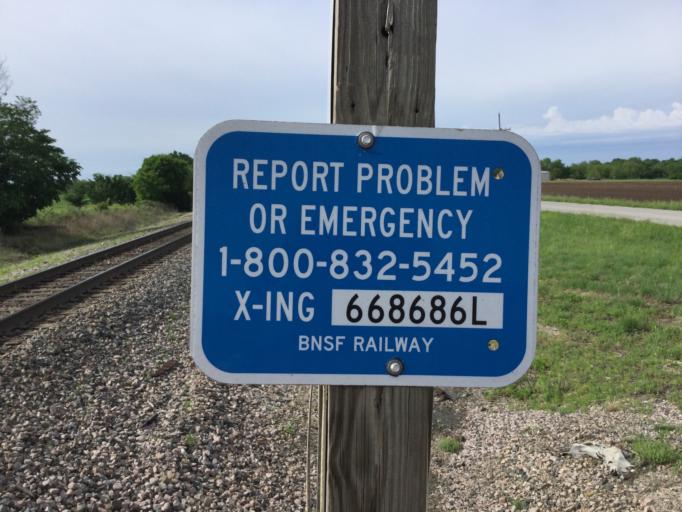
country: US
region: Kansas
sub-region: Linn County
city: Pleasanton
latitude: 38.0517
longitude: -94.6952
